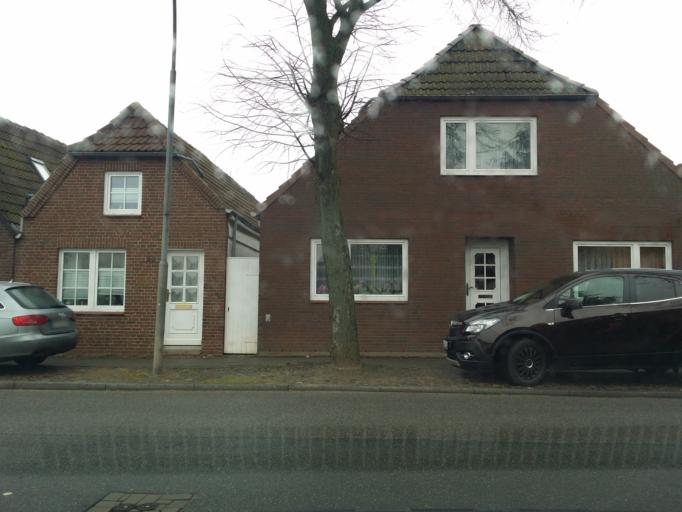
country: DE
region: Schleswig-Holstein
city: Burg auf Fehmarn
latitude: 54.4337
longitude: 11.1978
